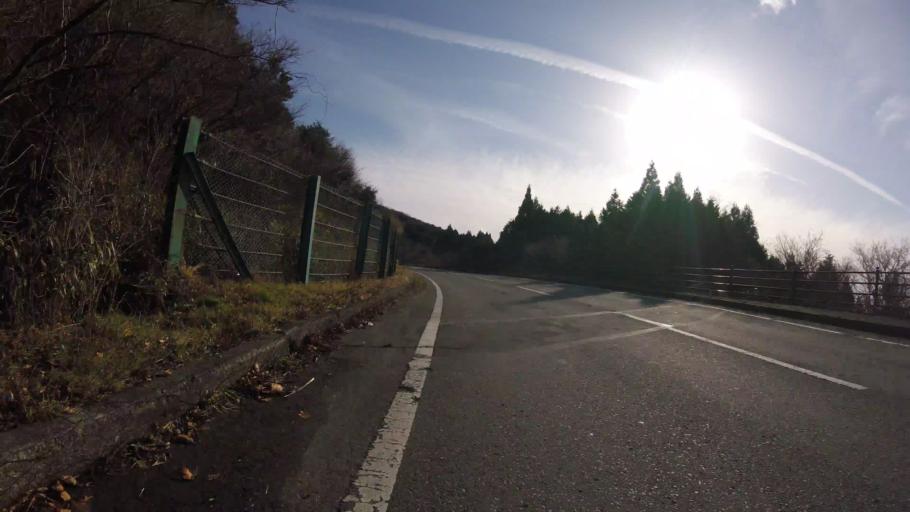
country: JP
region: Kanagawa
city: Hakone
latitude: 35.1740
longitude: 139.0215
